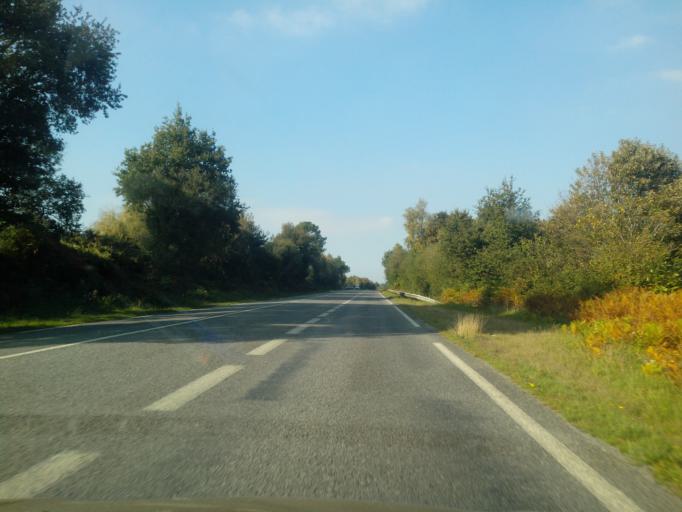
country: FR
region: Brittany
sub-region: Departement du Morbihan
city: Molac
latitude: 47.7258
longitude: -2.4405
